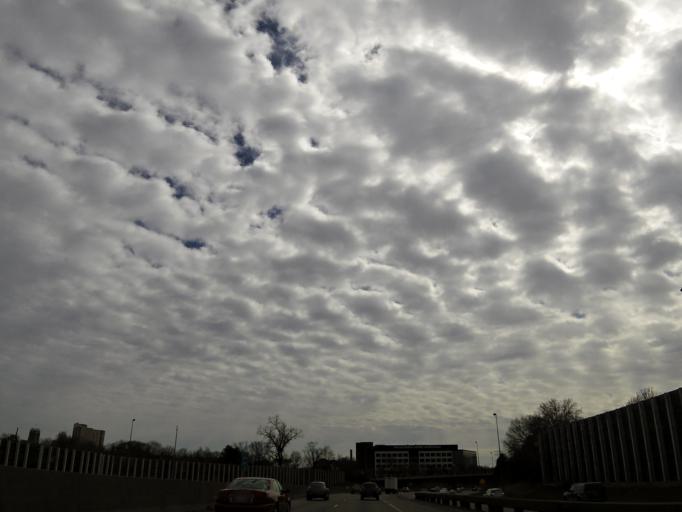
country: US
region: Minnesota
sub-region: Hennepin County
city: Minneapolis
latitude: 44.9582
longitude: -93.2697
